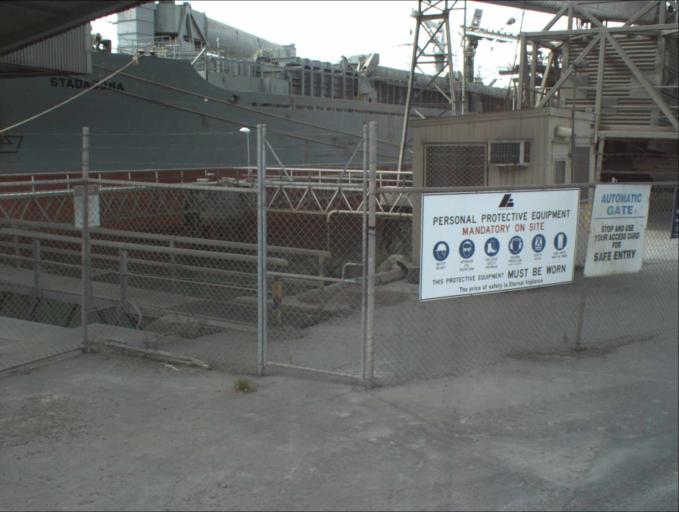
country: AU
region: South Australia
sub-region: Port Adelaide Enfield
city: Birkenhead
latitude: -34.8328
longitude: 138.5060
